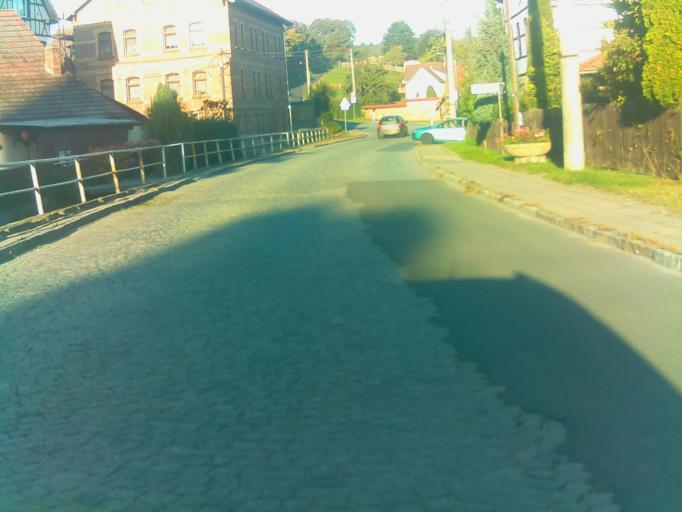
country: DE
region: Thuringia
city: Unterbodnitz
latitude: 50.8116
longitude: 11.6584
